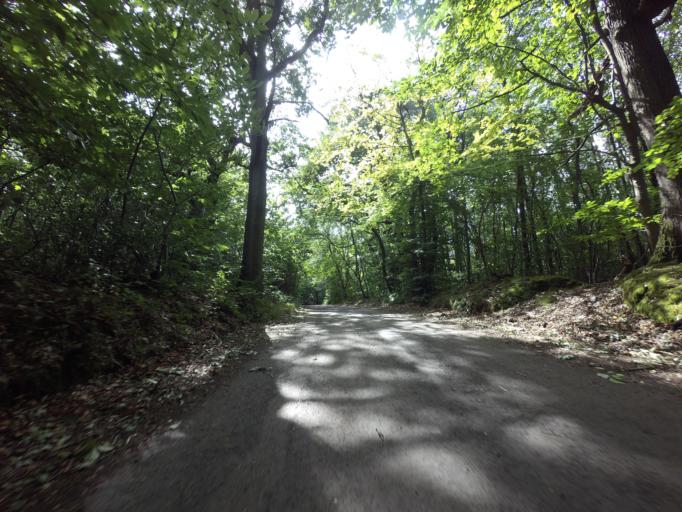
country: GB
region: England
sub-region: Kent
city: Halstead
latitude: 51.3486
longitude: 0.1416
